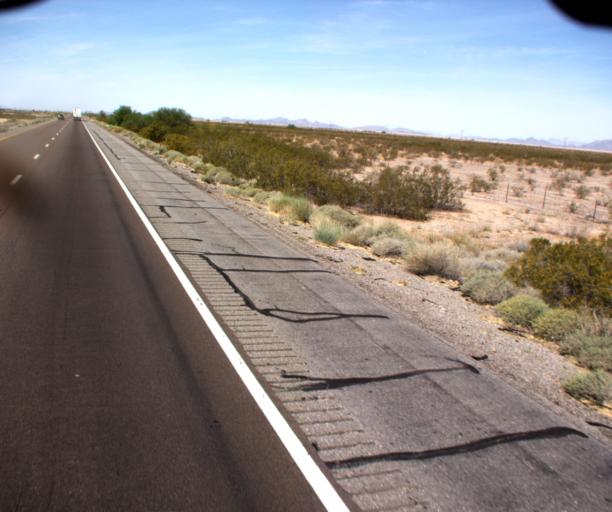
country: US
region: Arizona
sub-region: La Paz County
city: Salome
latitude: 33.5640
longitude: -113.3183
